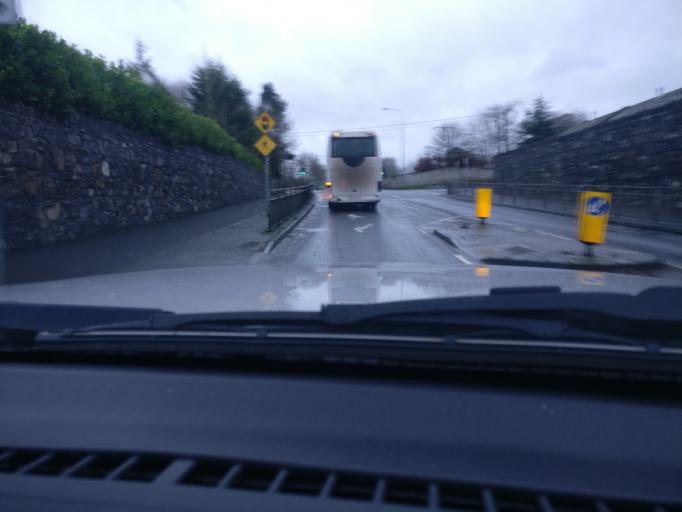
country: IE
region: Leinster
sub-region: An Mhi
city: Trim
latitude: 53.5521
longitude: -6.7868
